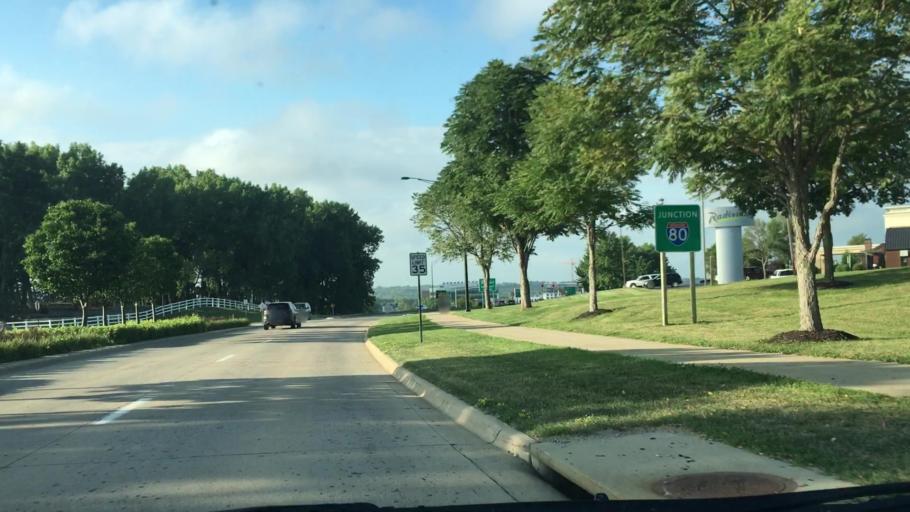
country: US
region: Iowa
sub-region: Johnson County
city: Coralville
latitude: 41.6892
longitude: -91.5644
